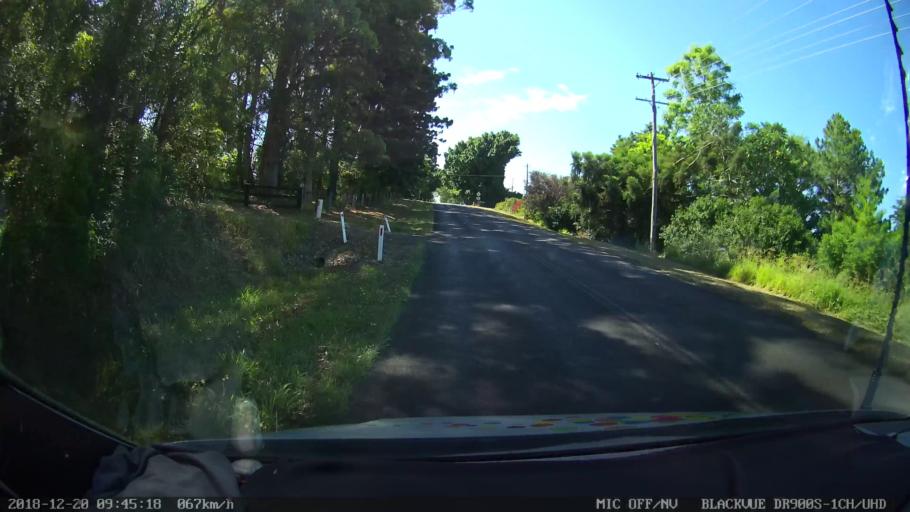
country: AU
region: New South Wales
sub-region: Lismore Municipality
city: Lismore
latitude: -28.7428
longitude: 153.2990
